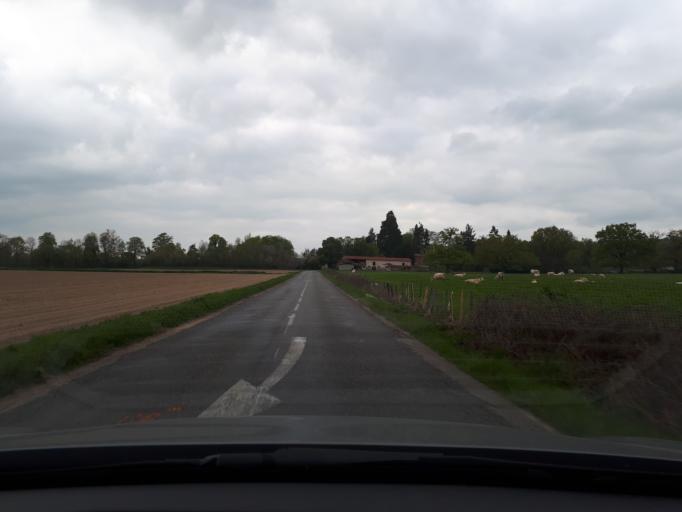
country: FR
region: Rhone-Alpes
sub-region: Departement de la Loire
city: Bellegarde-en-Forez
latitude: 45.7104
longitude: 4.2988
